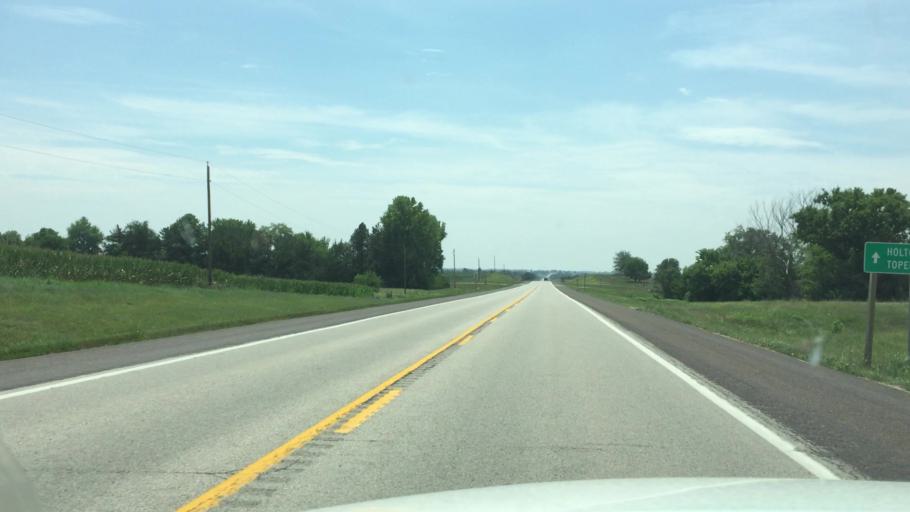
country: US
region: Kansas
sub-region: Jackson County
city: Holton
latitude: 39.6118
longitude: -95.7313
